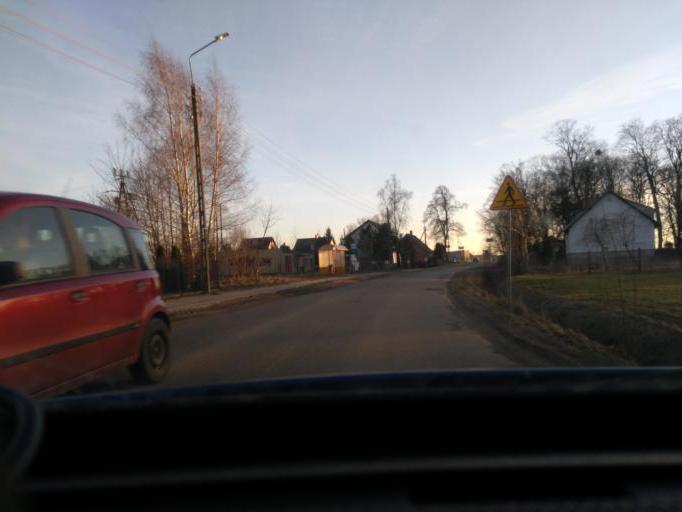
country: PL
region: Pomeranian Voivodeship
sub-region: Powiat kartuski
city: Przodkowo
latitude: 54.4009
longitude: 18.3318
